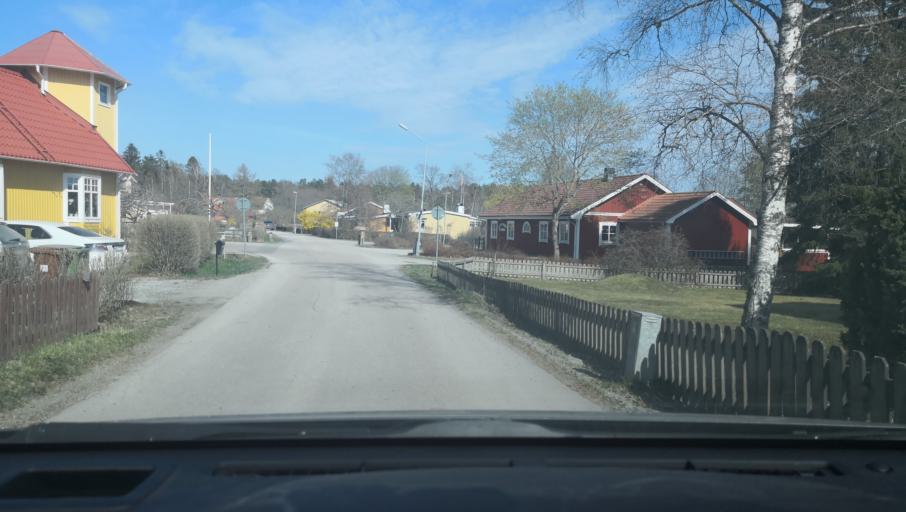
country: SE
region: Uppsala
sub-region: Enkopings Kommun
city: Irsta
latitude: 59.7747
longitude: 16.9282
